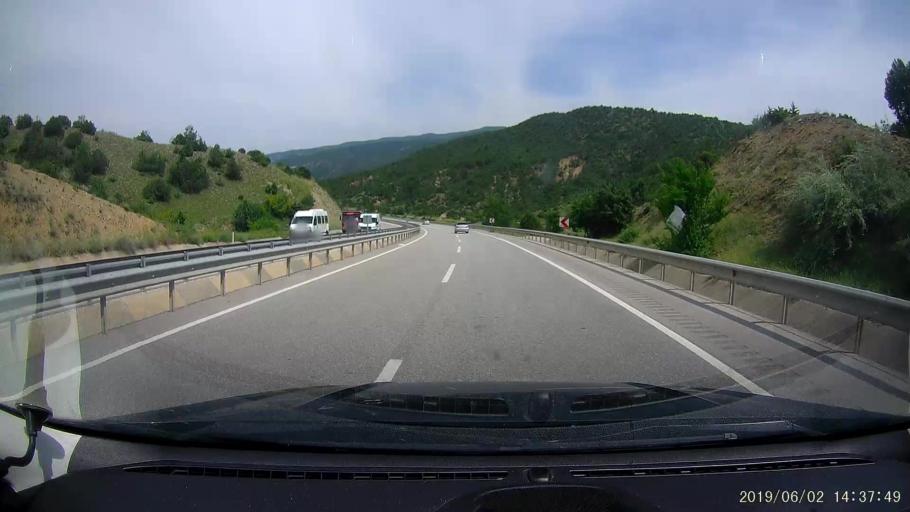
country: TR
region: Corum
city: Hacihamza
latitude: 41.0507
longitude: 34.2656
